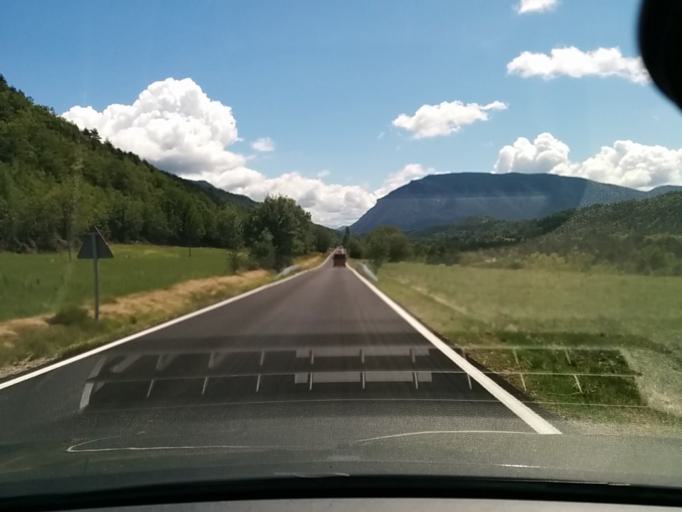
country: ES
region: Aragon
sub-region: Provincia de Huesca
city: Fiscal
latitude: 42.4767
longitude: -0.0629
